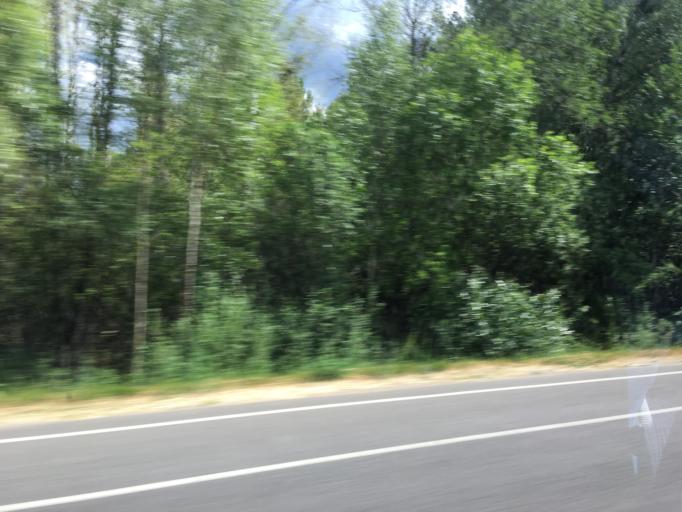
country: LT
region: Alytaus apskritis
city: Druskininkai
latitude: 53.8758
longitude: 24.1236
